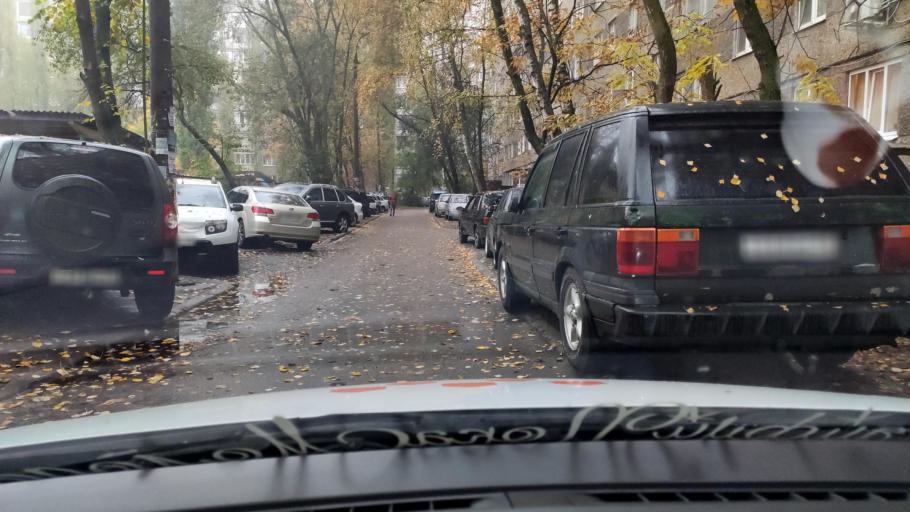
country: RU
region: Voronezj
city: Podgornoye
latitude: 51.7089
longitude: 39.1644
